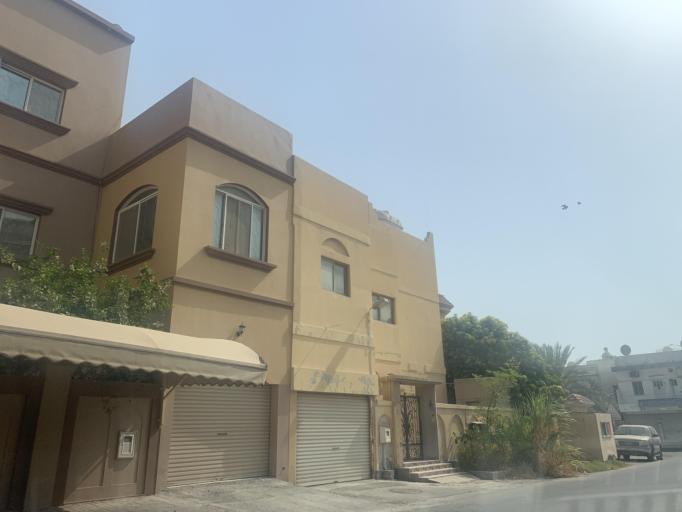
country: BH
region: Manama
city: Jidd Hafs
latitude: 26.2138
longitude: 50.4660
